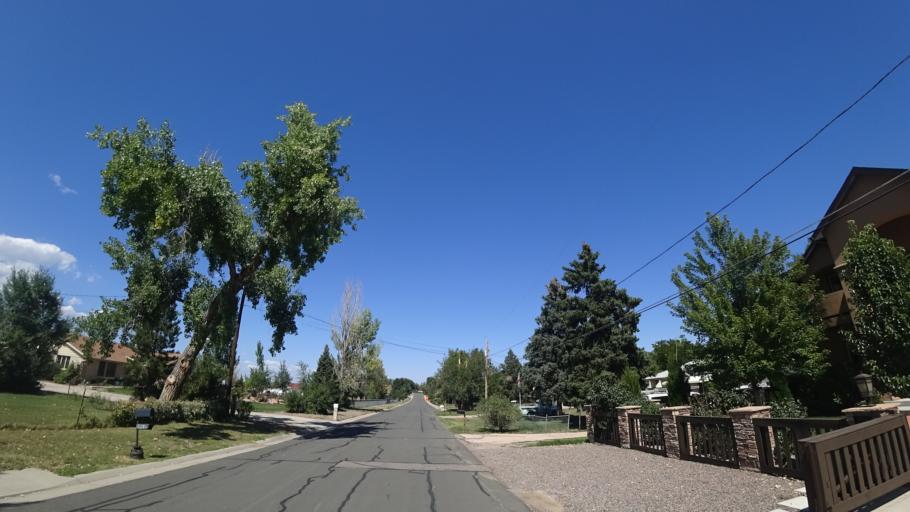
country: US
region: Colorado
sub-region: Arapahoe County
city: Littleton
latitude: 39.6046
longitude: -104.9846
